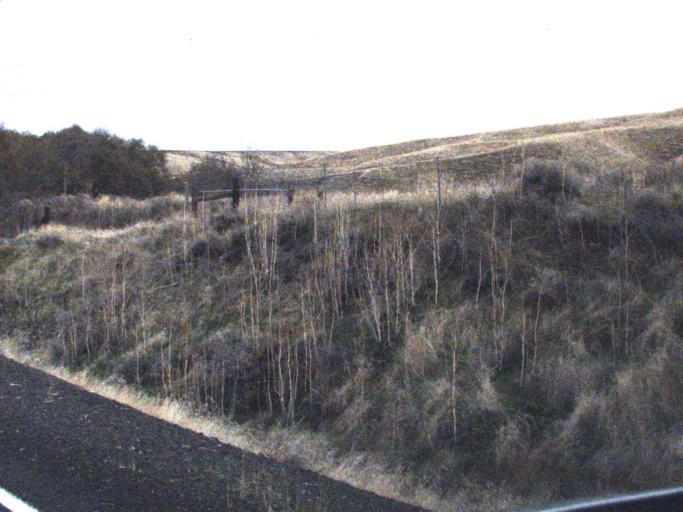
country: US
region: Washington
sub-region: Walla Walla County
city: Waitsburg
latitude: 46.5427
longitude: -118.1618
